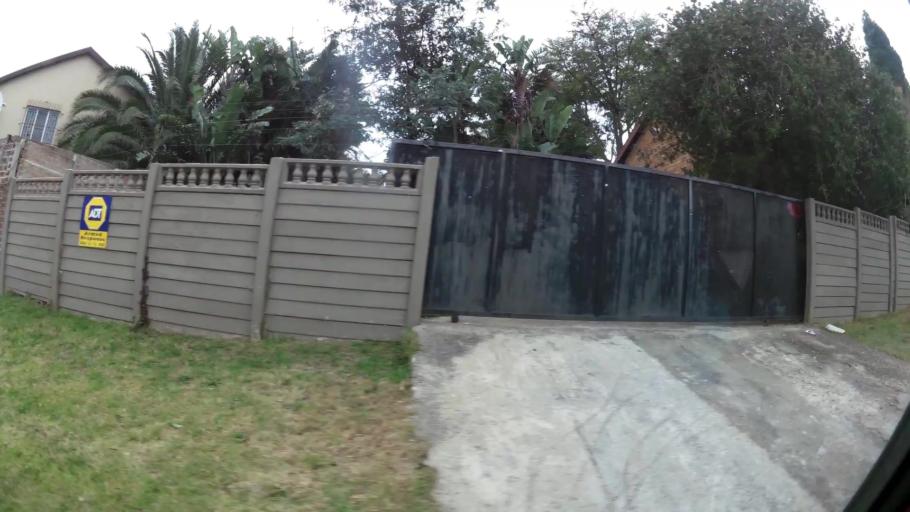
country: ZA
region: Gauteng
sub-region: City of Johannesburg Metropolitan Municipality
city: Roodepoort
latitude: -26.1133
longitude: 27.9061
